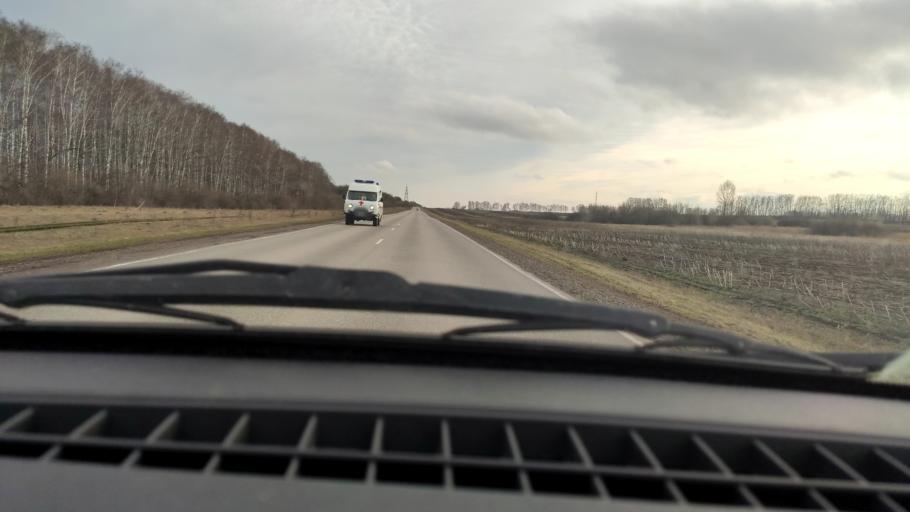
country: RU
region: Bashkortostan
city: Chishmy
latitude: 54.4892
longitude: 55.2742
